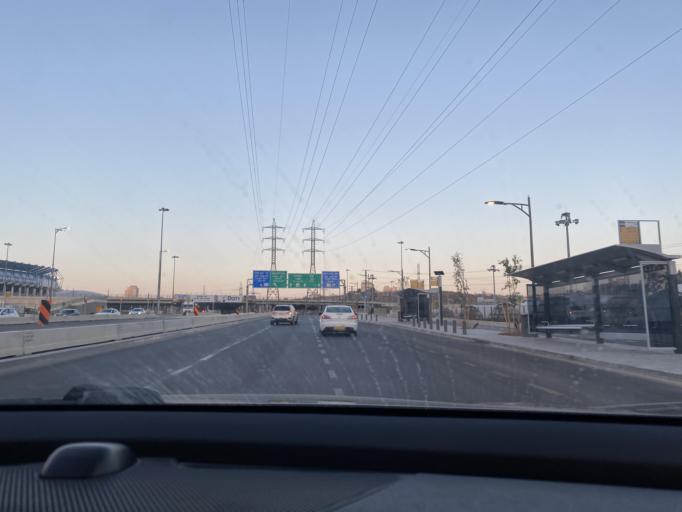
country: PS
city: Khallat Hamamah
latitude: 31.7486
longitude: 35.1871
